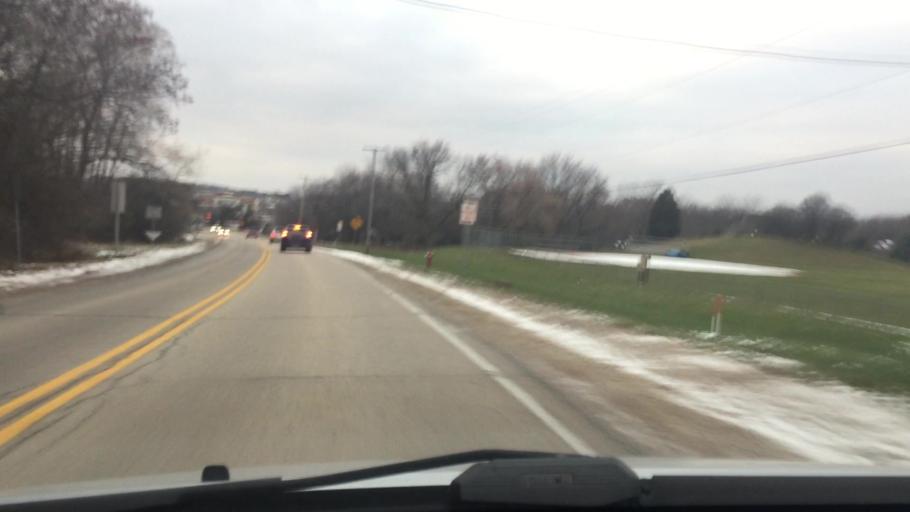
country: US
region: Wisconsin
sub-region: Waukesha County
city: Delafield
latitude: 43.0515
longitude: -88.3611
